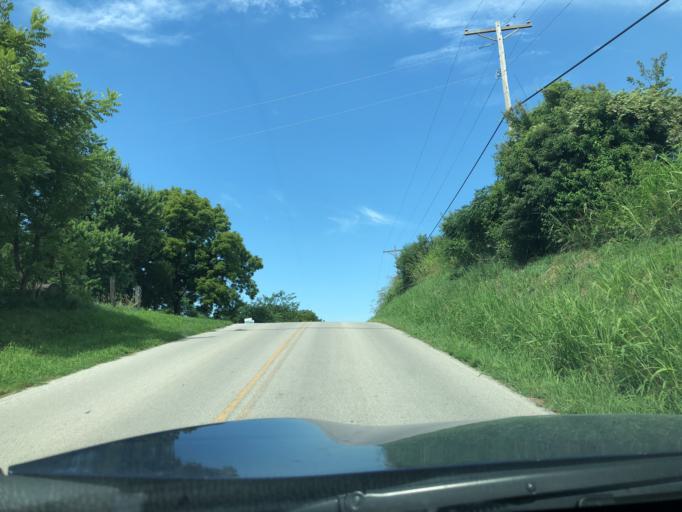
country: US
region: Missouri
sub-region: Platte County
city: Platte City
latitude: 39.3318
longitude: -94.8411
